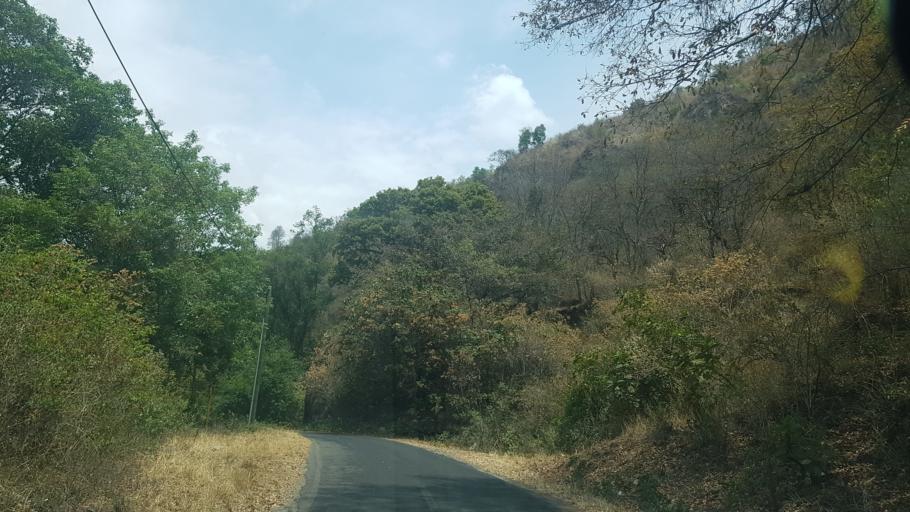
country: MX
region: Puebla
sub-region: Tochimilco
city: La Magdalena Yancuitlalpan
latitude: 18.8762
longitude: -98.6107
